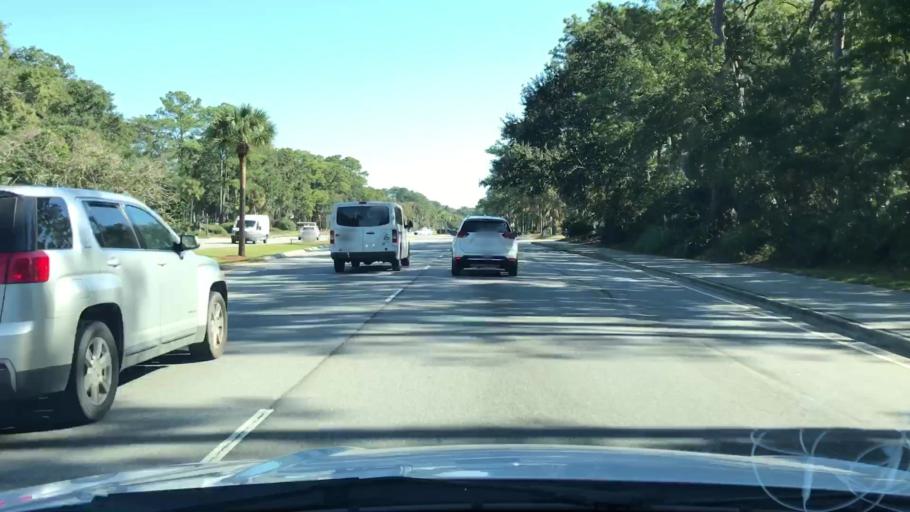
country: US
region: South Carolina
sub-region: Beaufort County
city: Hilton Head Island
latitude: 32.2160
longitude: -80.7071
